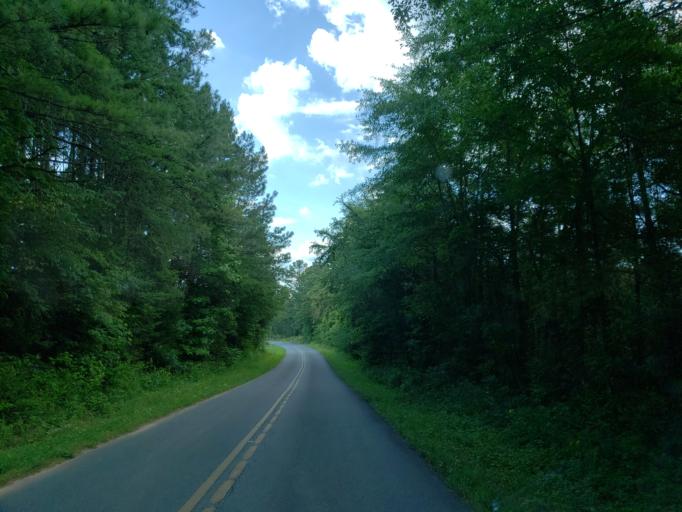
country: US
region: Georgia
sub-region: Polk County
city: Cedartown
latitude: 33.9242
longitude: -85.2701
